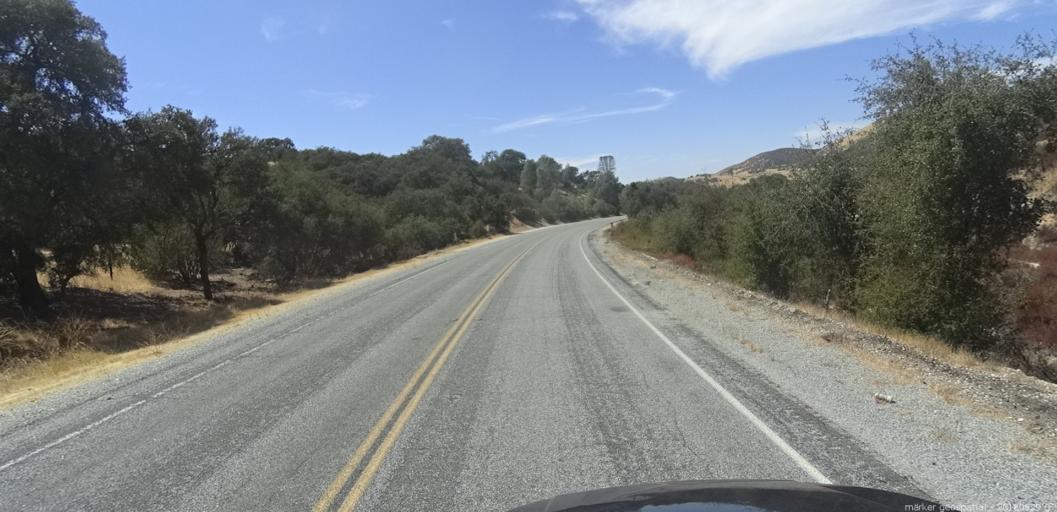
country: US
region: California
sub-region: San Luis Obispo County
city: Lake Nacimiento
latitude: 35.9028
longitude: -120.9736
